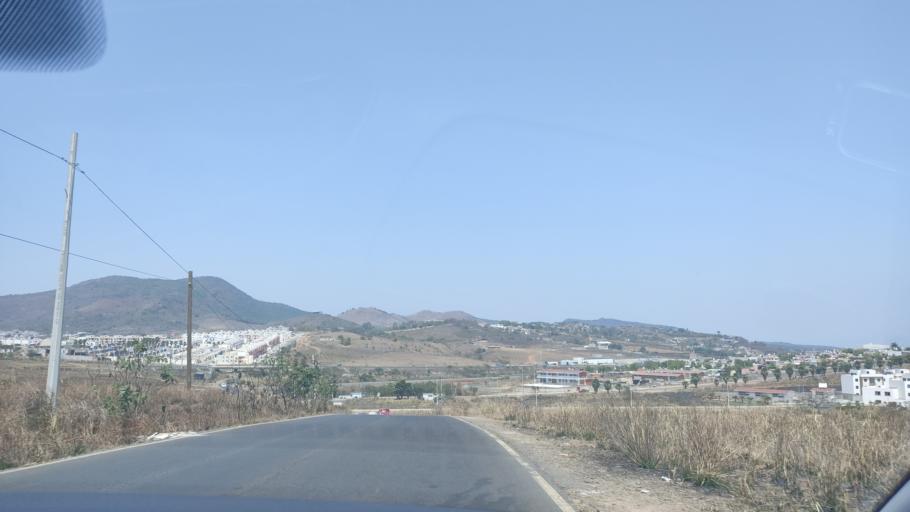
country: MX
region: Nayarit
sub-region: Tepic
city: La Corregidora
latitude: 21.4907
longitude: -104.8097
